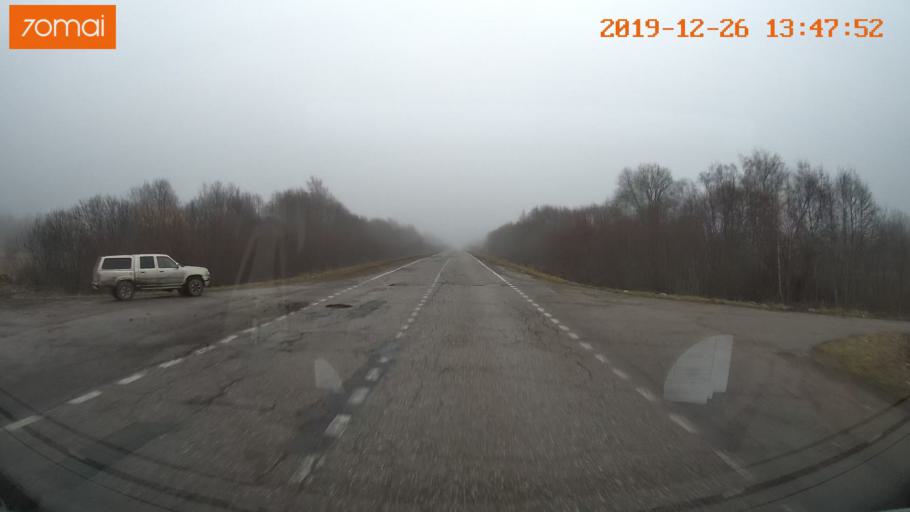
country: RU
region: Vologda
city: Sheksna
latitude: 58.6814
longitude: 38.5395
